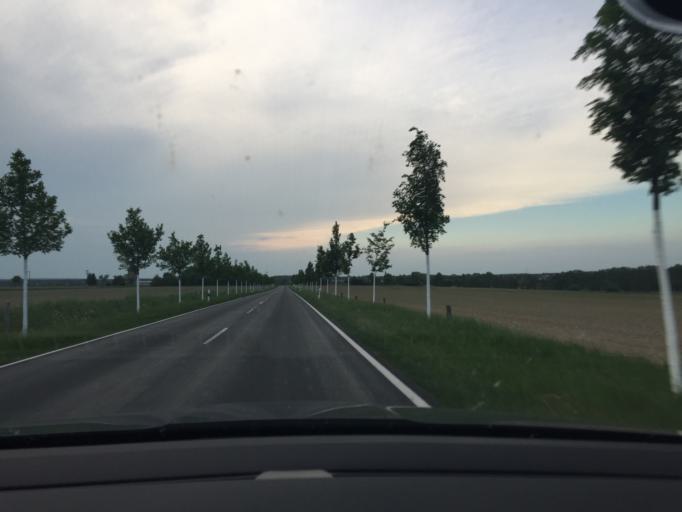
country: DE
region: Brandenburg
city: Niemegk
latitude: 52.0544
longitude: 12.6986
